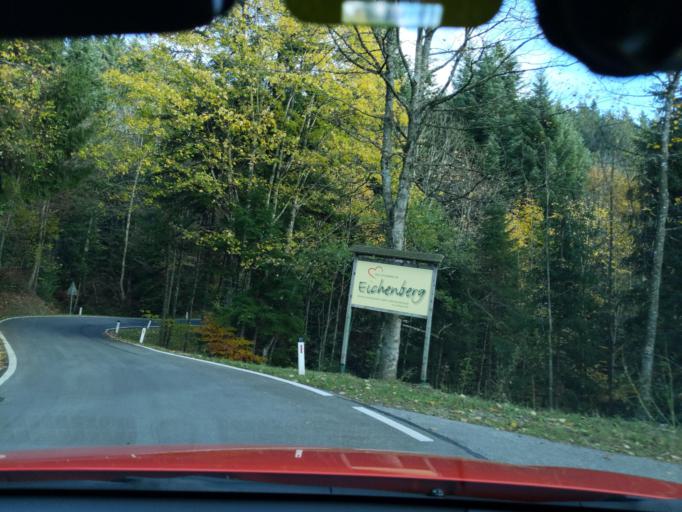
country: AT
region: Vorarlberg
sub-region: Politischer Bezirk Bregenz
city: Eichenberg
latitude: 47.5515
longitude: 9.7857
